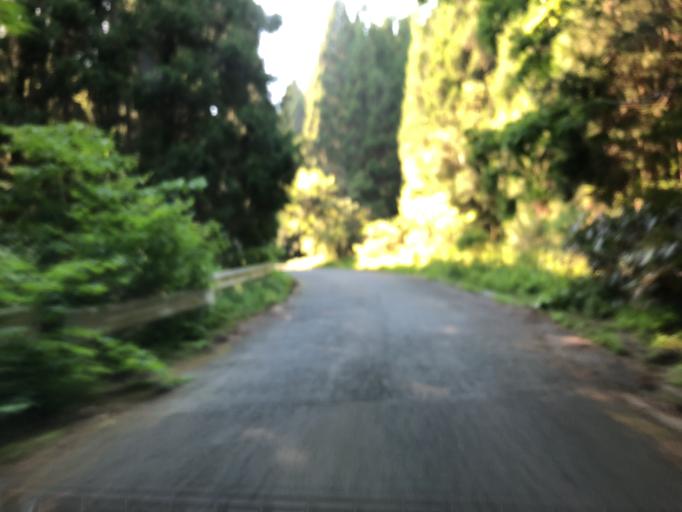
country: JP
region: Ibaraki
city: Kitaibaraki
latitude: 36.8683
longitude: 140.6801
